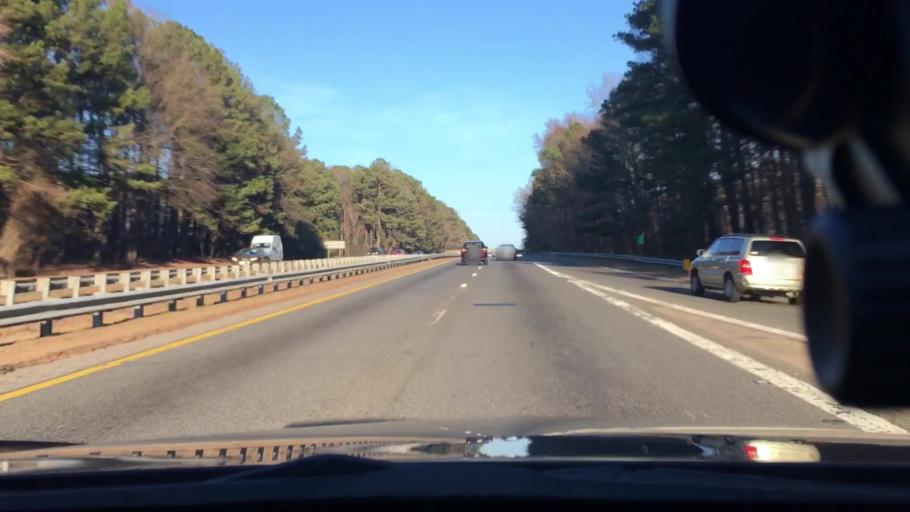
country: US
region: North Carolina
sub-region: Wake County
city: West Raleigh
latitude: 35.7720
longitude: -78.7198
